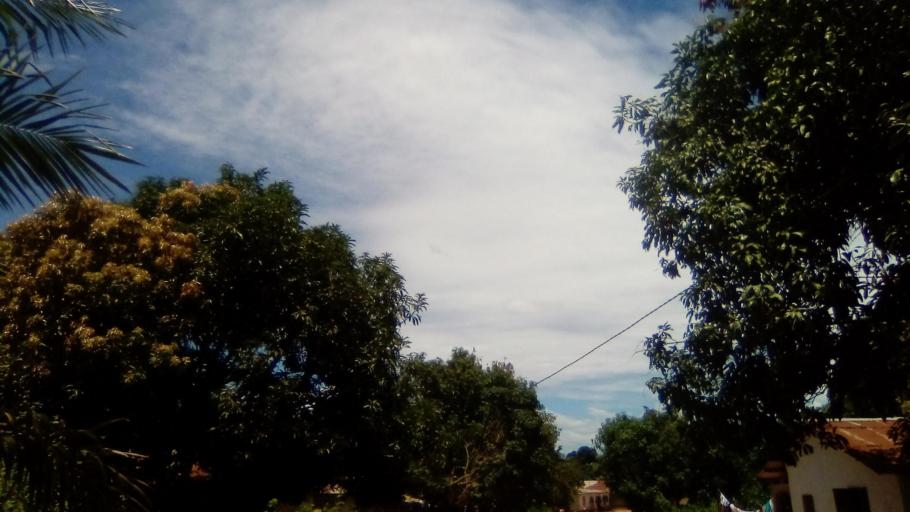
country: SL
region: Eastern Province
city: Simbakoro
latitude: 8.6260
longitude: -10.9880
